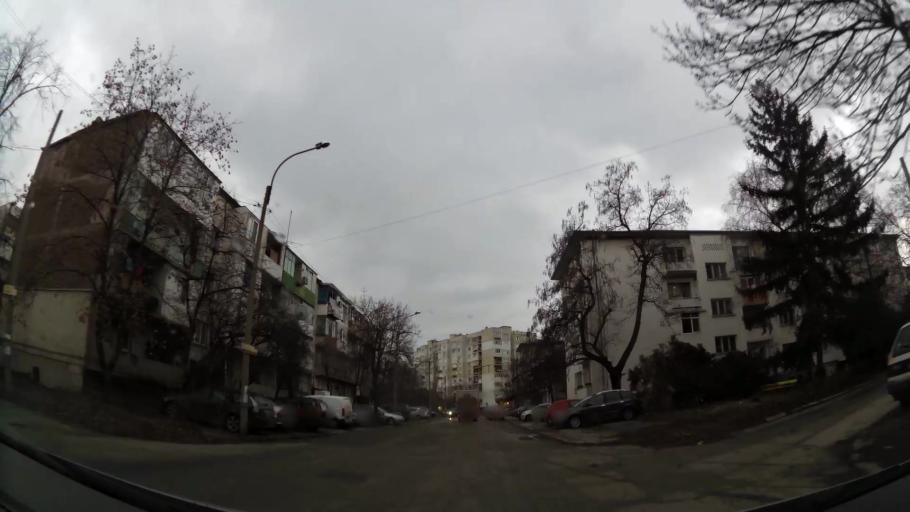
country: BG
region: Sofia-Capital
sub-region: Stolichna Obshtina
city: Sofia
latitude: 42.7343
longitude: 23.3001
